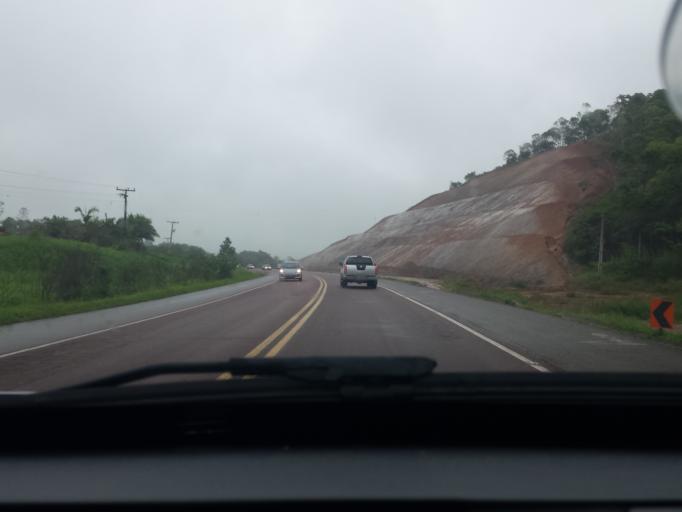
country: BR
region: Santa Catarina
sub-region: Itajai
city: Itajai
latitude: -26.8397
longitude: -48.7887
